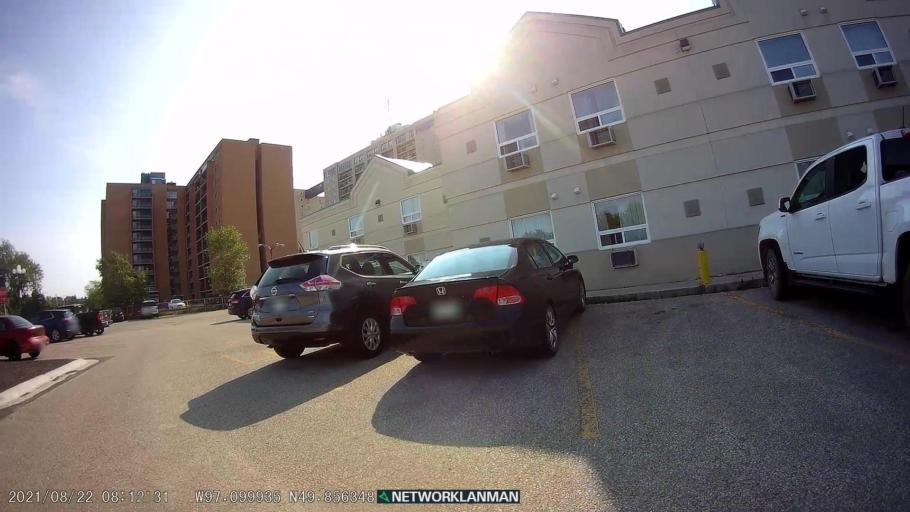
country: CA
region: Manitoba
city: Winnipeg
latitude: 49.8583
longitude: -97.1000
